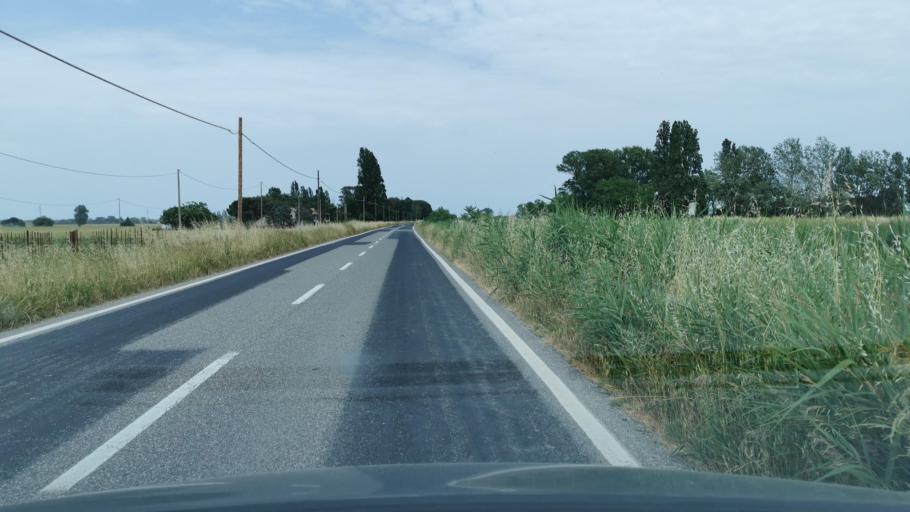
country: IT
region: Emilia-Romagna
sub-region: Provincia di Ravenna
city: Marina Romea
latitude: 44.5559
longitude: 12.2311
